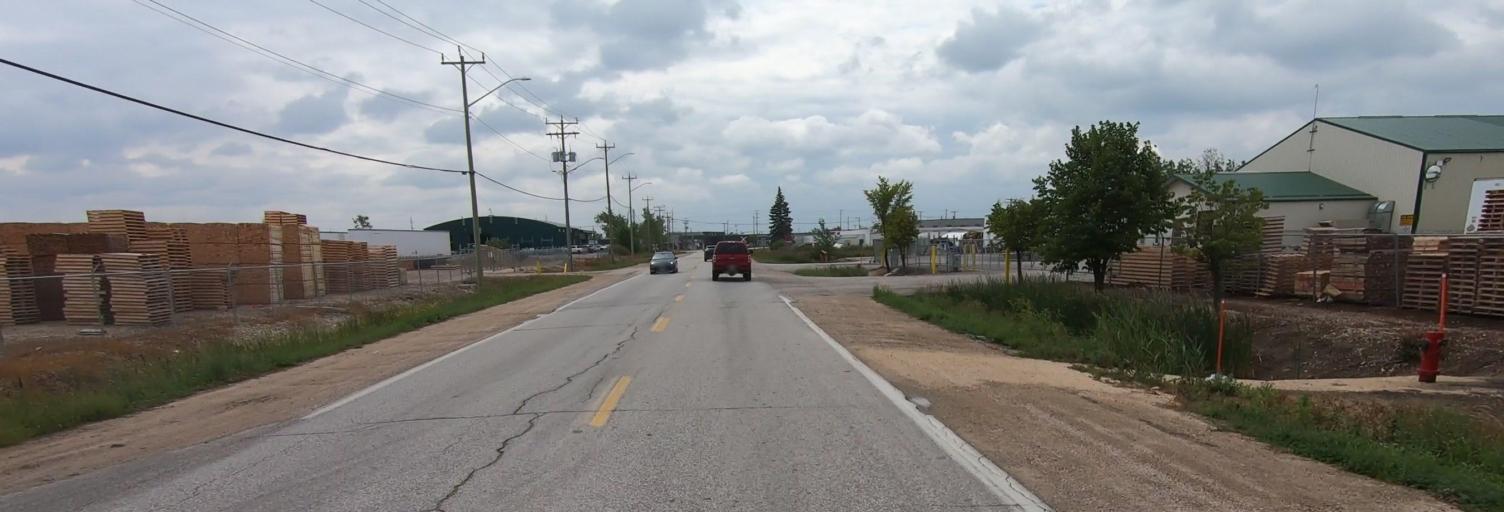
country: CA
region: Manitoba
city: Winnipeg
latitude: 49.8886
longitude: -97.0791
